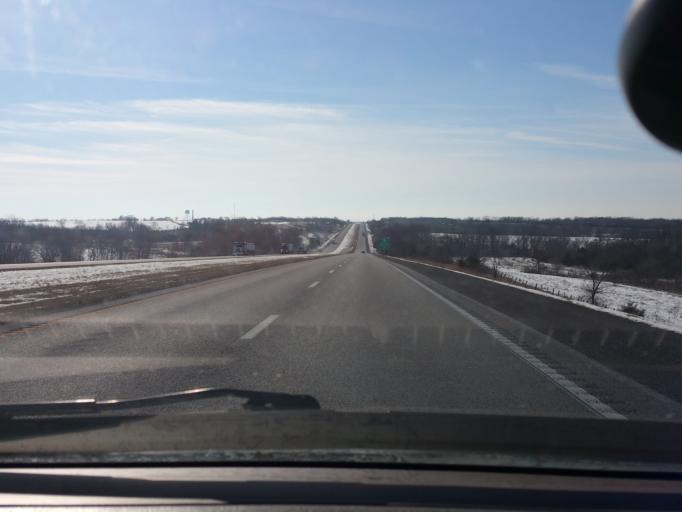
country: US
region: Missouri
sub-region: Daviess County
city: Gallatin
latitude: 39.9187
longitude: -94.1412
